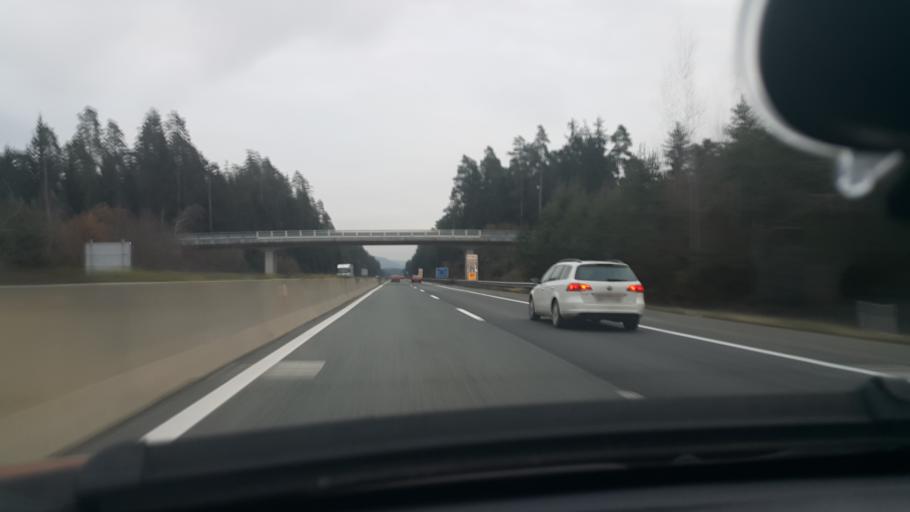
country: AT
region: Carinthia
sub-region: Politischer Bezirk Klagenfurt Land
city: Poggersdorf
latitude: 46.6389
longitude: 14.4626
